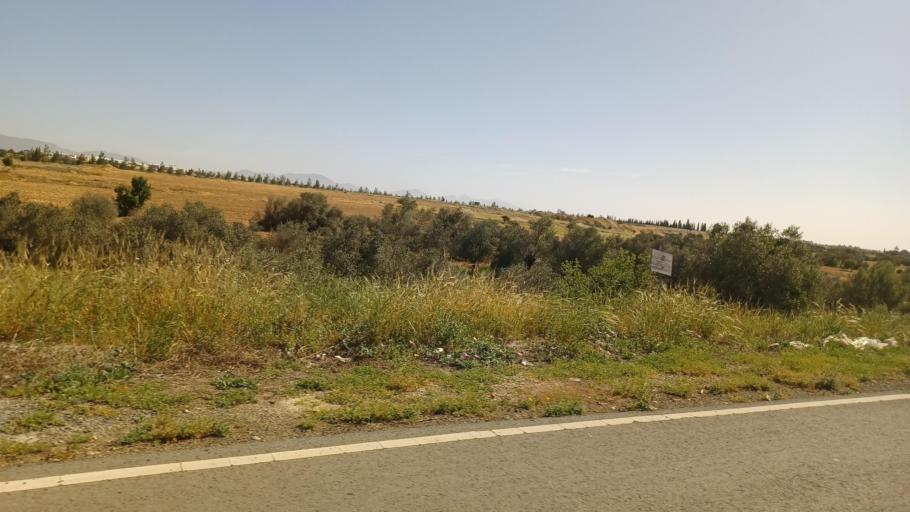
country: CY
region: Lefkosia
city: Kokkinotrimithia
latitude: 35.1569
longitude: 33.1855
